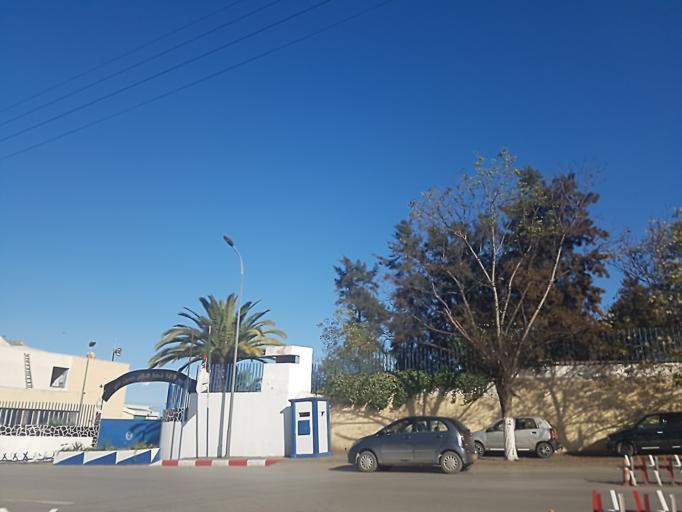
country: DZ
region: Alger
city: Birkhadem
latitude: 36.7336
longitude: 3.1044
